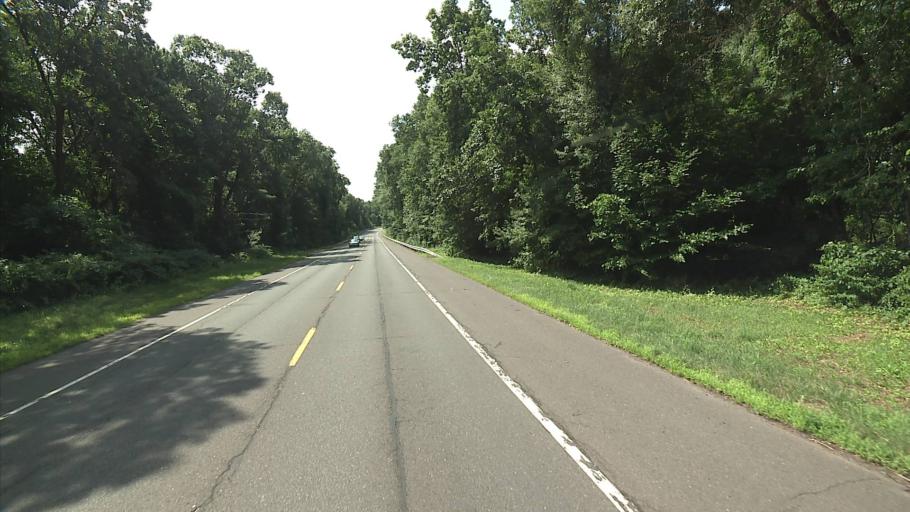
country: US
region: Connecticut
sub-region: Hartford County
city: Glastonbury Center
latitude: 41.6917
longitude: -72.5995
